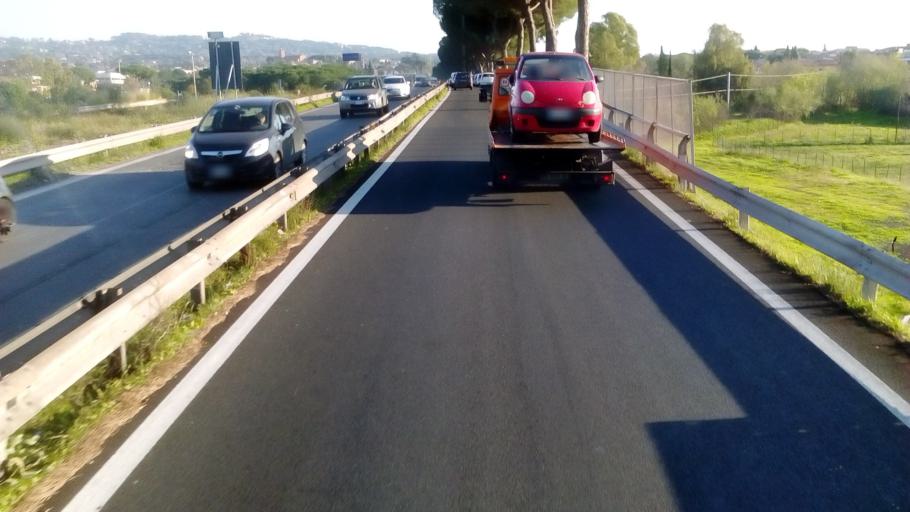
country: IT
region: Latium
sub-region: Citta metropolitana di Roma Capitale
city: Ciampino
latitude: 41.7779
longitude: 12.6059
